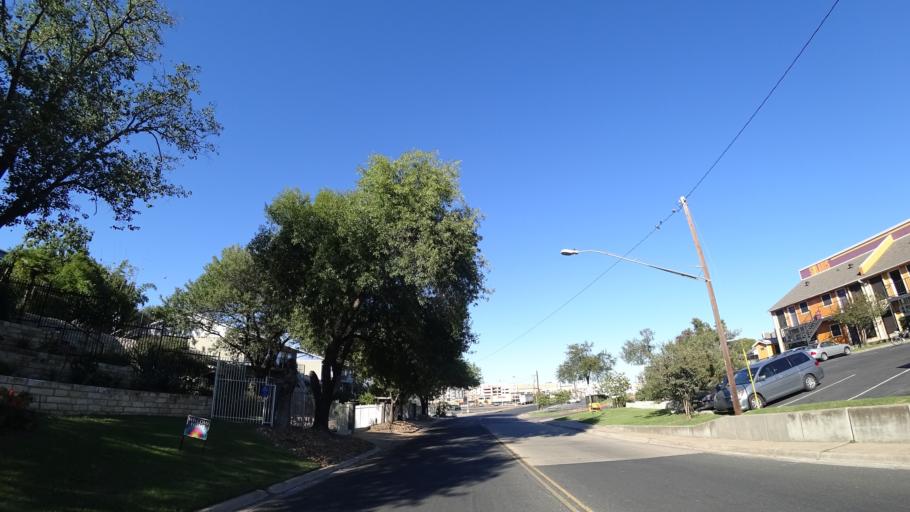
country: US
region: Texas
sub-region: Travis County
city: Austin
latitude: 30.2404
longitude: -97.7299
